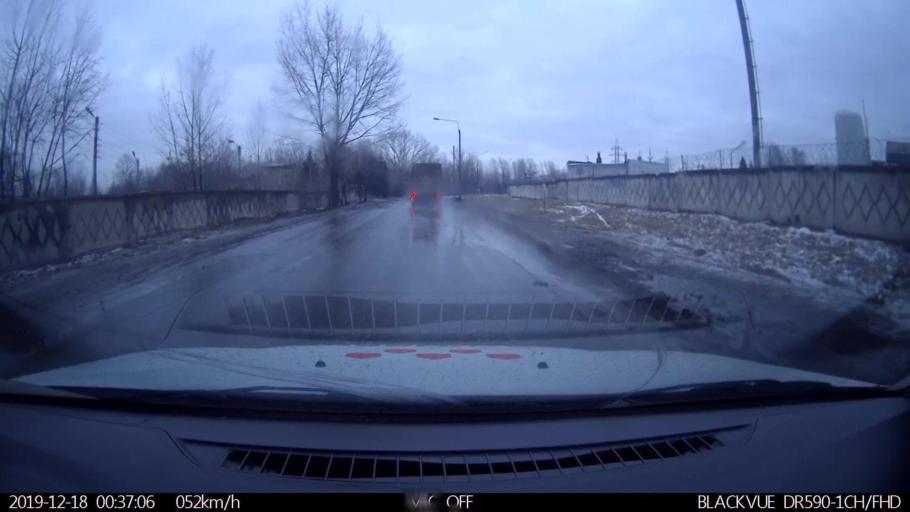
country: RU
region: Nizjnij Novgorod
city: Neklyudovo
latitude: 56.3549
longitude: 43.8943
